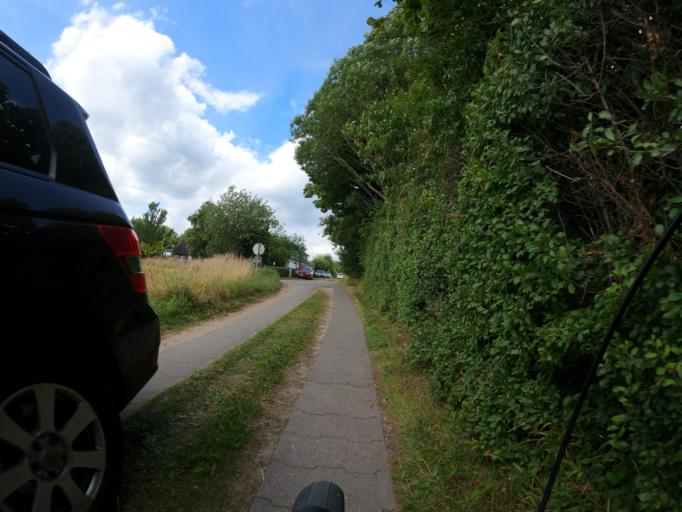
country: DE
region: Schleswig-Holstein
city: Steinberg
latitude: 54.7946
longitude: 9.7925
